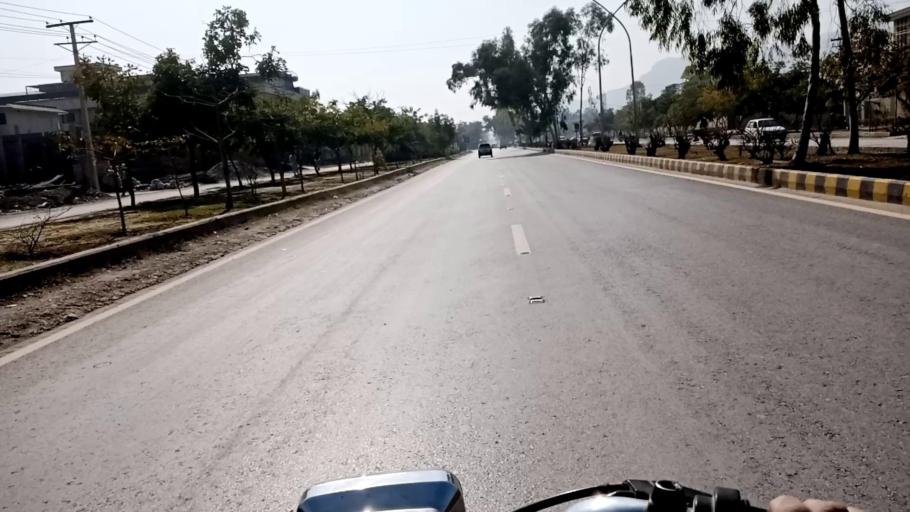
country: PK
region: Khyber Pakhtunkhwa
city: Peshawar
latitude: 33.9583
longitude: 71.4330
